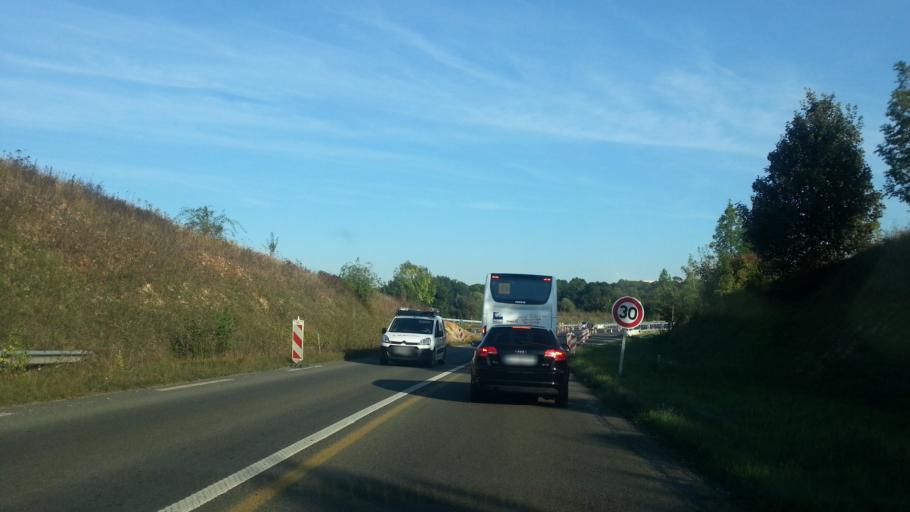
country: FR
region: Picardie
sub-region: Departement de l'Oise
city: Tille
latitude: 49.4600
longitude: 2.0870
